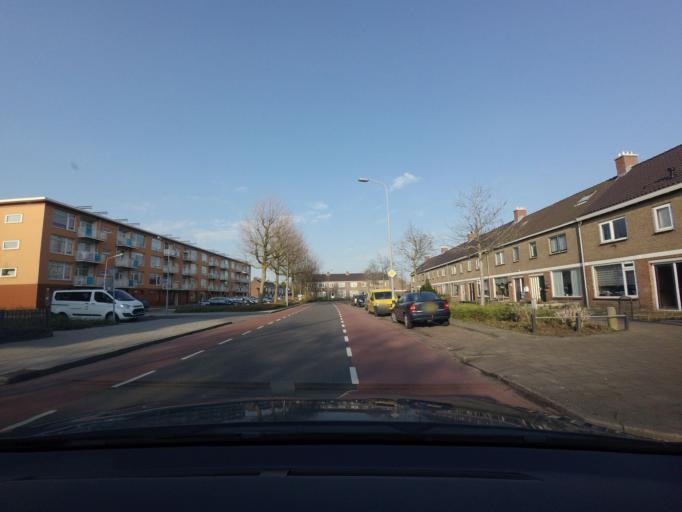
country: NL
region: North Holland
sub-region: Gemeente Heemskerk
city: Heemskerk
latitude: 52.5151
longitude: 4.6741
